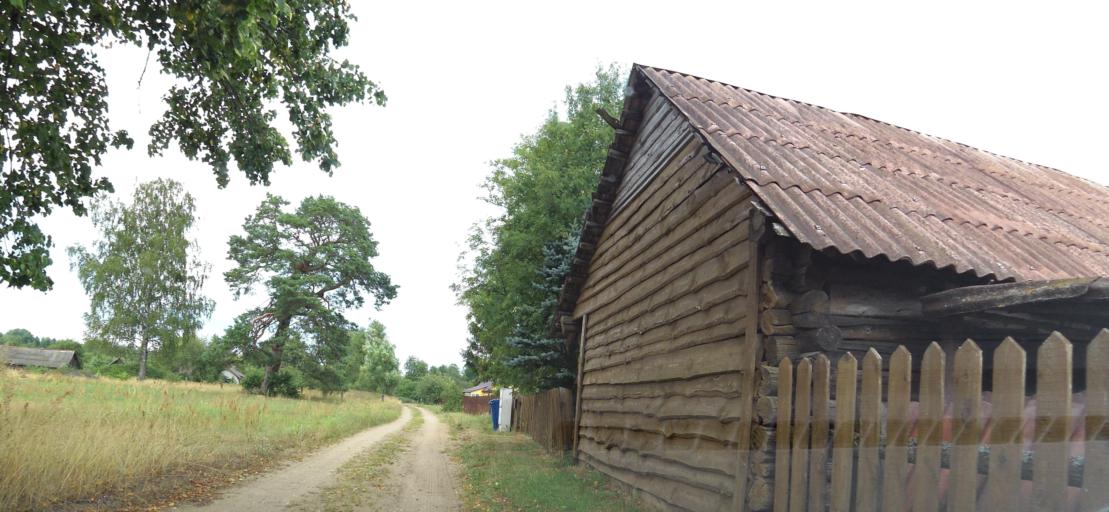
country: LT
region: Alytaus apskritis
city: Varena
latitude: 54.0193
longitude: 24.3331
